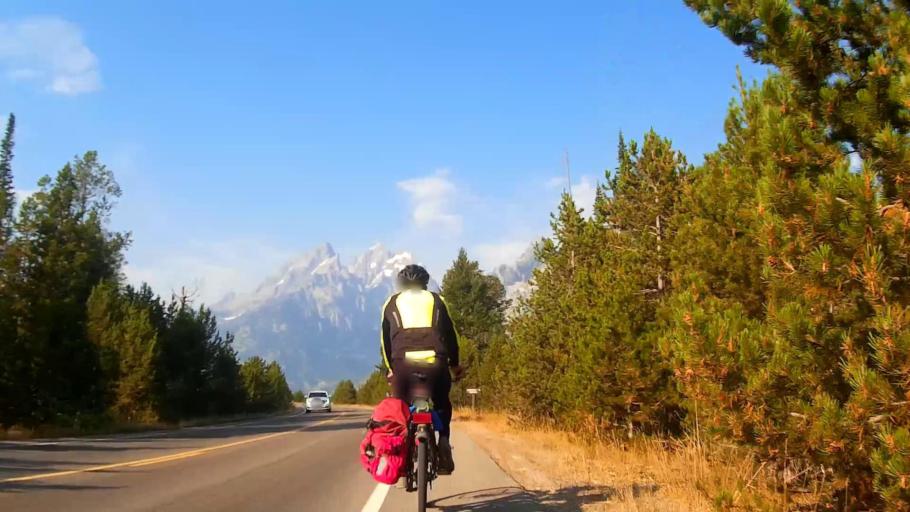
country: US
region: Wyoming
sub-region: Teton County
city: Moose Wilson Road
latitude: 43.7917
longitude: -110.7096
